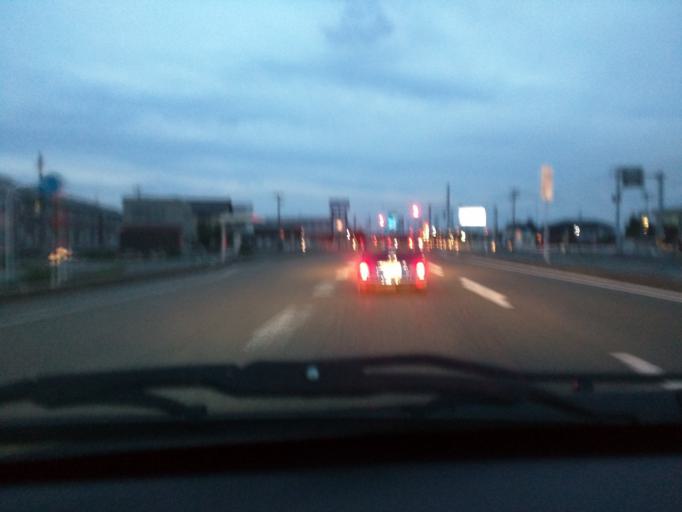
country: JP
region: Niigata
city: Kashiwazaki
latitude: 37.3620
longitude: 138.5858
